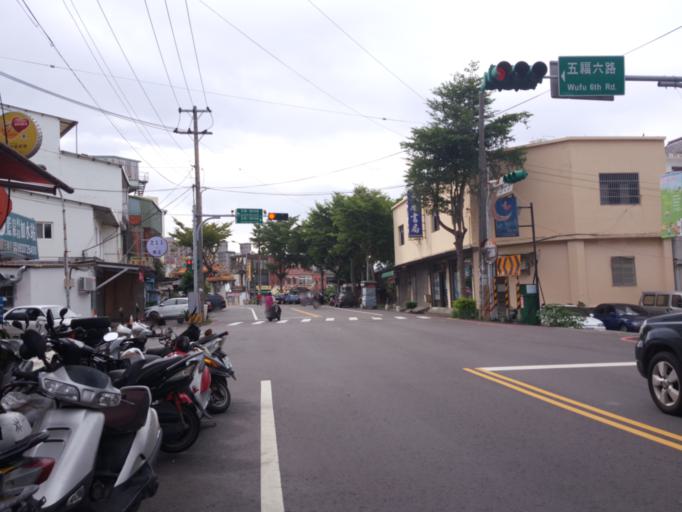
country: TW
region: Taiwan
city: Taoyuan City
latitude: 25.0545
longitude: 121.2945
